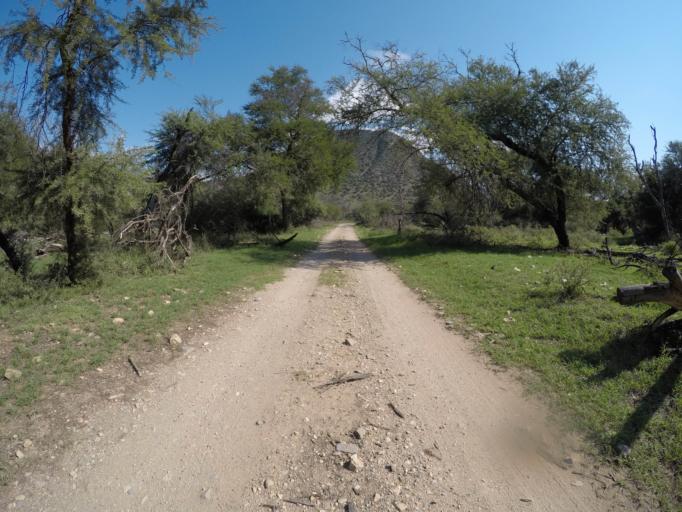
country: ZA
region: Eastern Cape
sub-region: Cacadu District Municipality
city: Kareedouw
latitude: -33.6672
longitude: 24.3830
